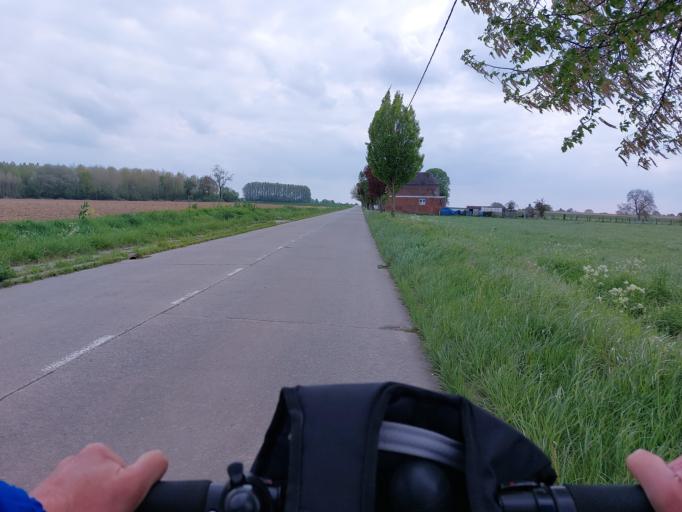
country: BE
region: Wallonia
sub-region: Province du Hainaut
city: Dour
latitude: 50.3592
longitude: 3.7368
